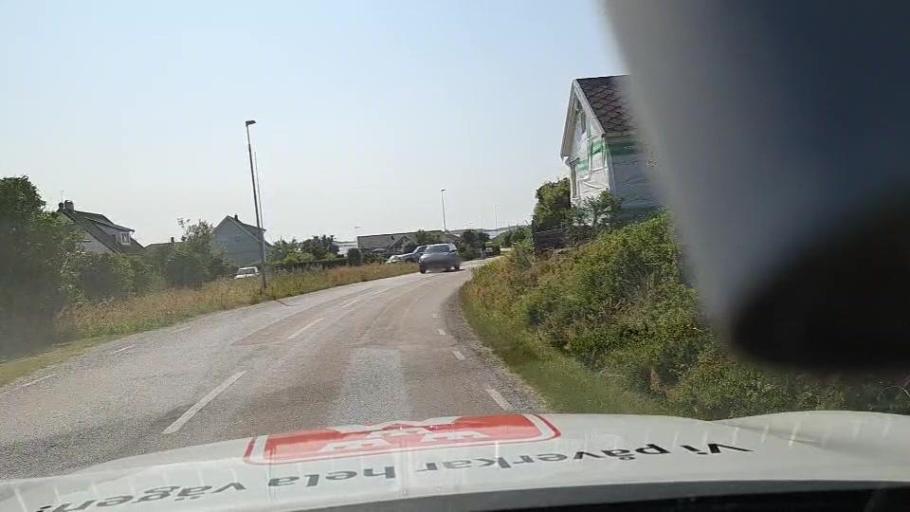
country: SE
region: Vaestra Goetaland
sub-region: Tjorns Kommun
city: Skaerhamn
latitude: 58.1069
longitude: 11.4757
